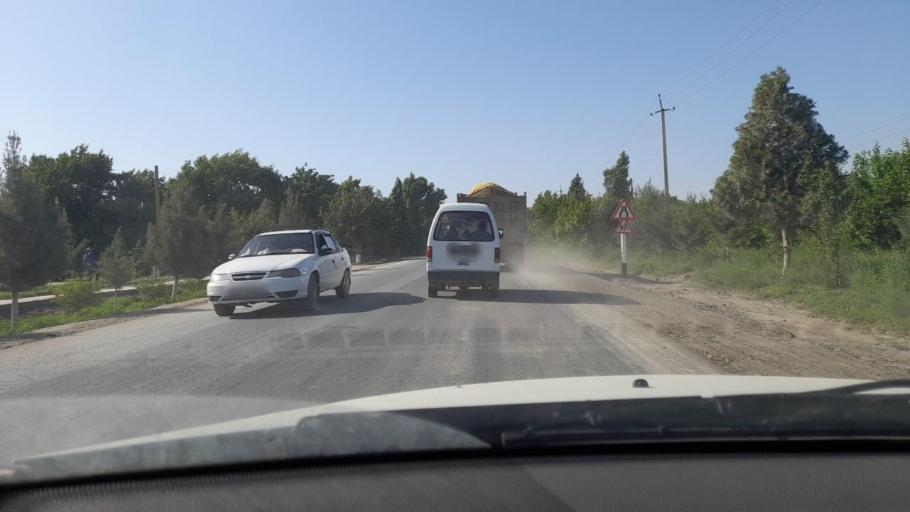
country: UZ
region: Bukhara
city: Romiton
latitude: 40.0500
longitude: 64.3285
